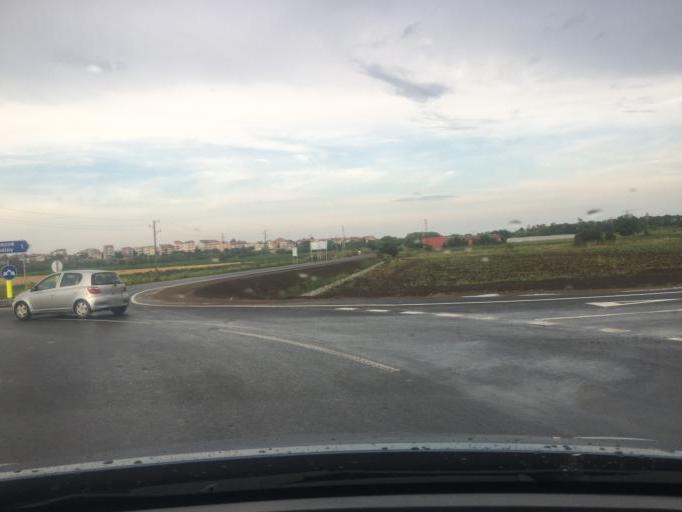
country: BG
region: Burgas
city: Aheloy
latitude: 42.6458
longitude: 27.6368
